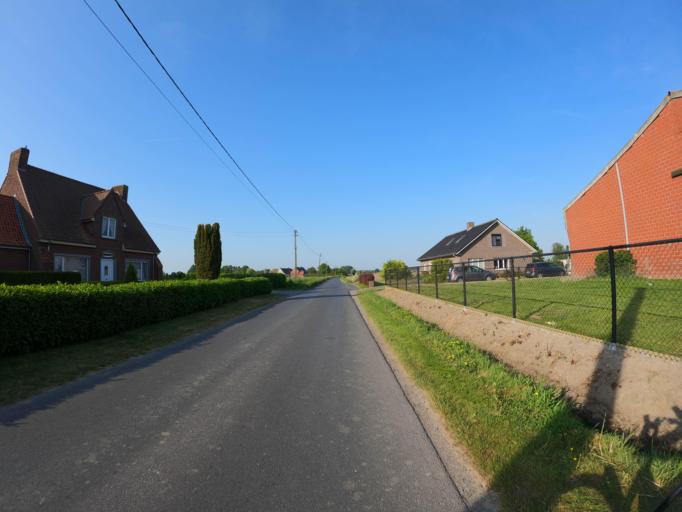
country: BE
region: Flanders
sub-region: Provincie West-Vlaanderen
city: Ruiselede
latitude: 51.0353
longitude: 3.3776
